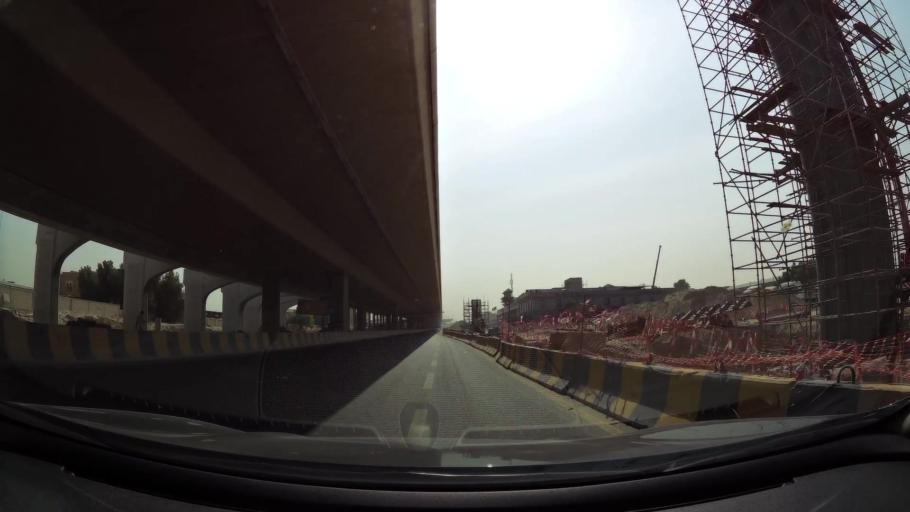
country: KW
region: Al Asimah
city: Ar Rabiyah
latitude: 29.3293
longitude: 47.9322
